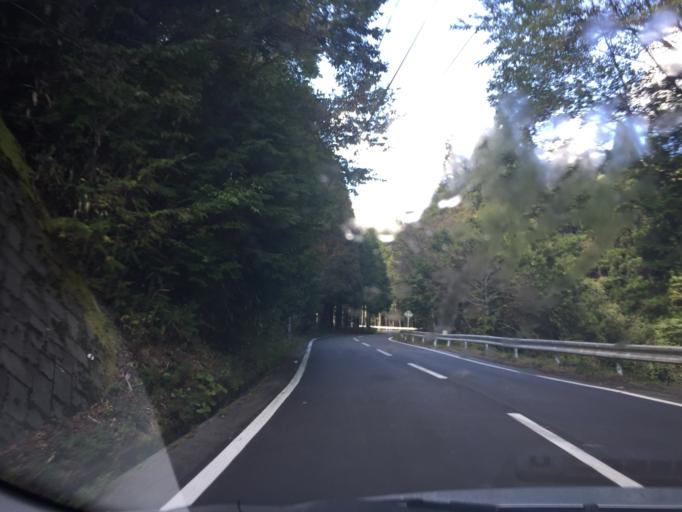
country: JP
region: Gifu
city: Nakatsugawa
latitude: 35.2974
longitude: 137.6788
